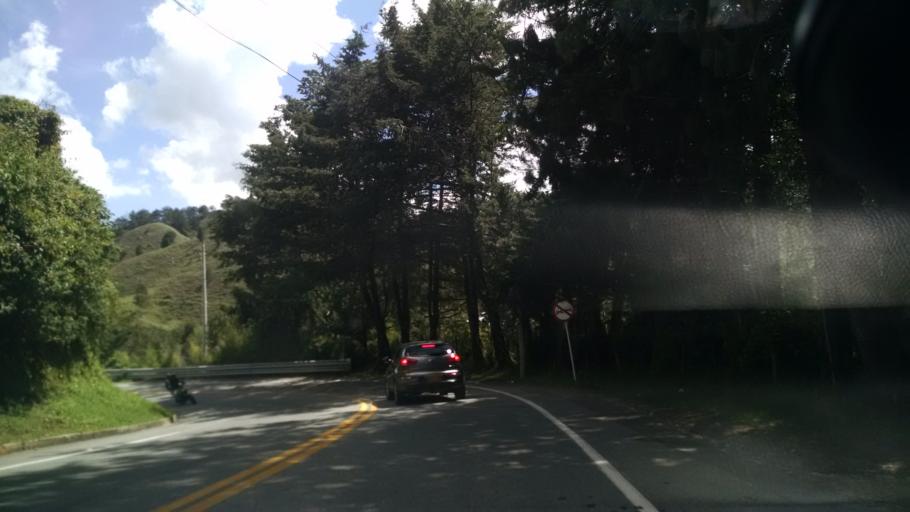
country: CO
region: Antioquia
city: El Retiro
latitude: 6.1327
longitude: -75.5068
